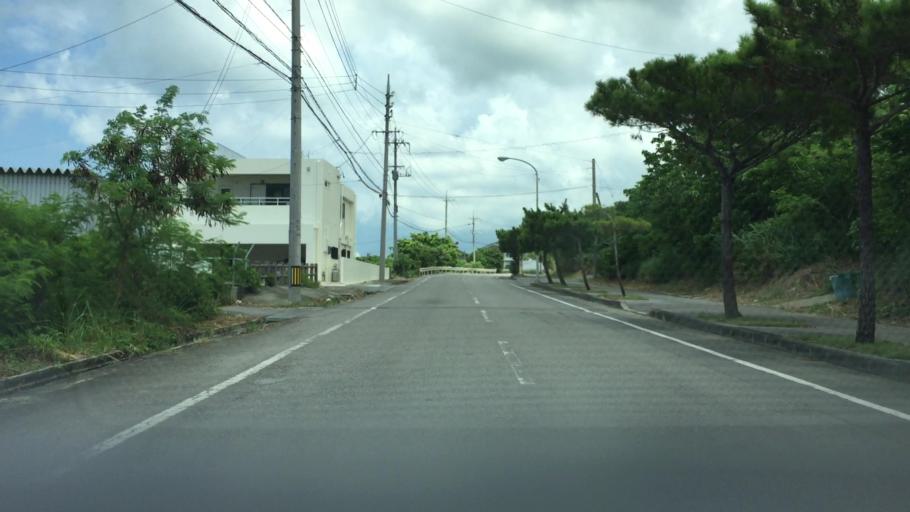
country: JP
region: Okinawa
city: Ishigaki
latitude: 24.3596
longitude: 124.1446
